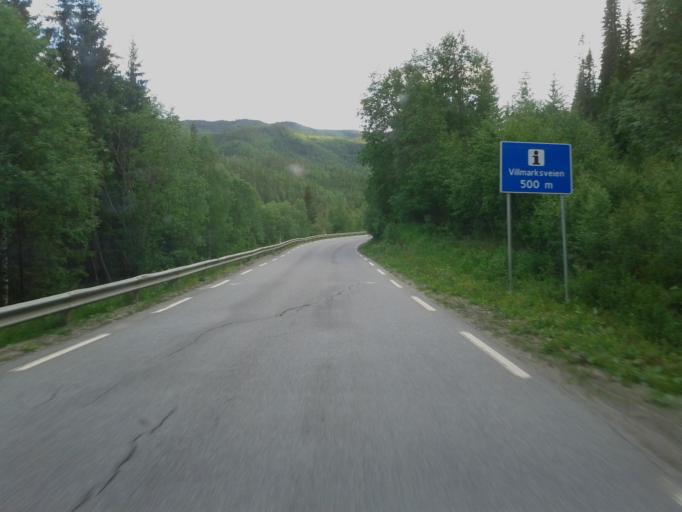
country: NO
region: Nordland
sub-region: Grane
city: Trofors
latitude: 65.5206
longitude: 13.6346
